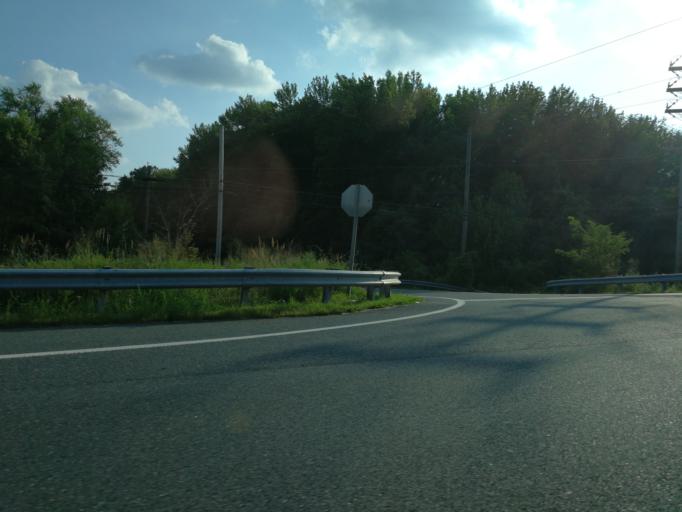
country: US
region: Maryland
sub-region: Harford County
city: Perryman
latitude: 39.4902
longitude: -76.2017
